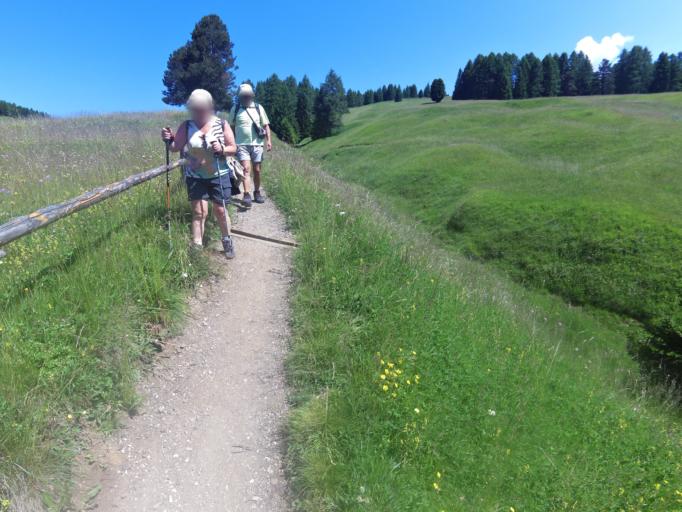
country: IT
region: Trentino-Alto Adige
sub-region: Bolzano
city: Ortisei
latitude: 46.5372
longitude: 11.6686
